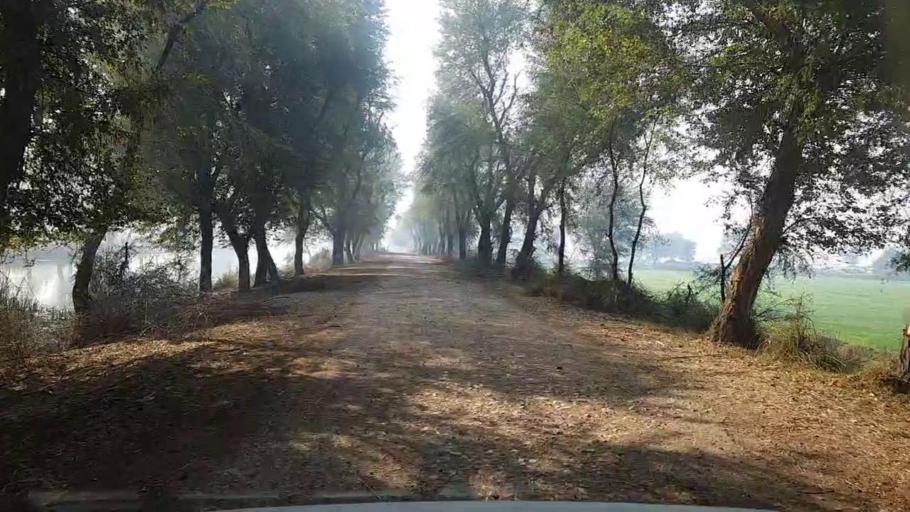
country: PK
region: Sindh
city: Khairpur
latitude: 27.9531
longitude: 69.6527
